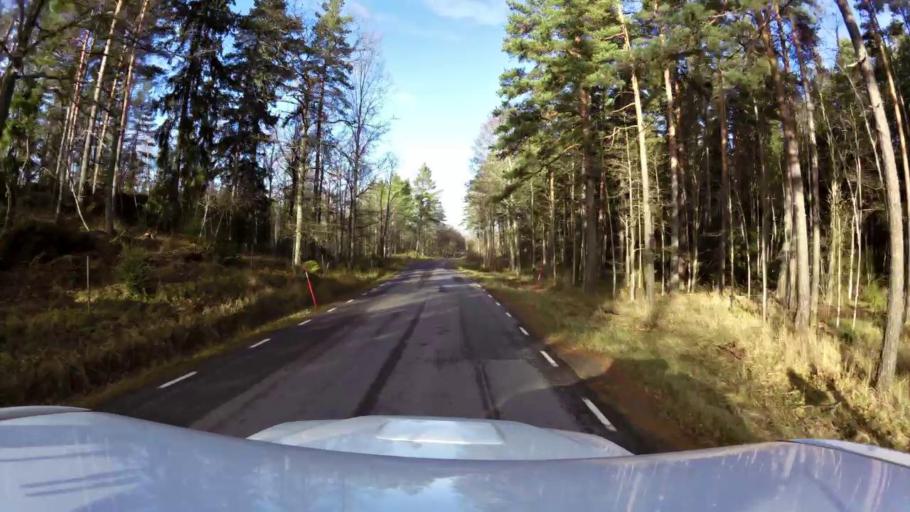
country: SE
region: OEstergoetland
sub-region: Linkopings Kommun
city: Linkoping
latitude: 58.3755
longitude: 15.6240
